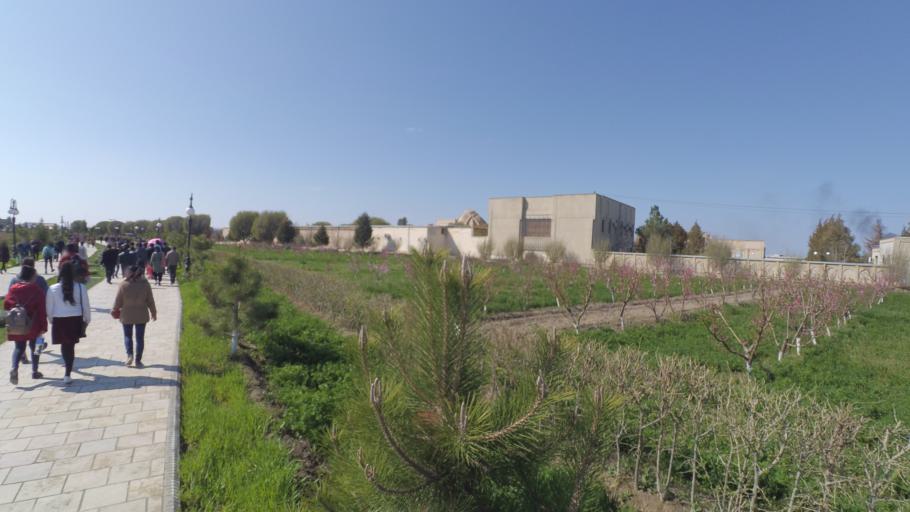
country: UZ
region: Bukhara
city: Kogon
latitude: 39.8028
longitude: 64.5388
